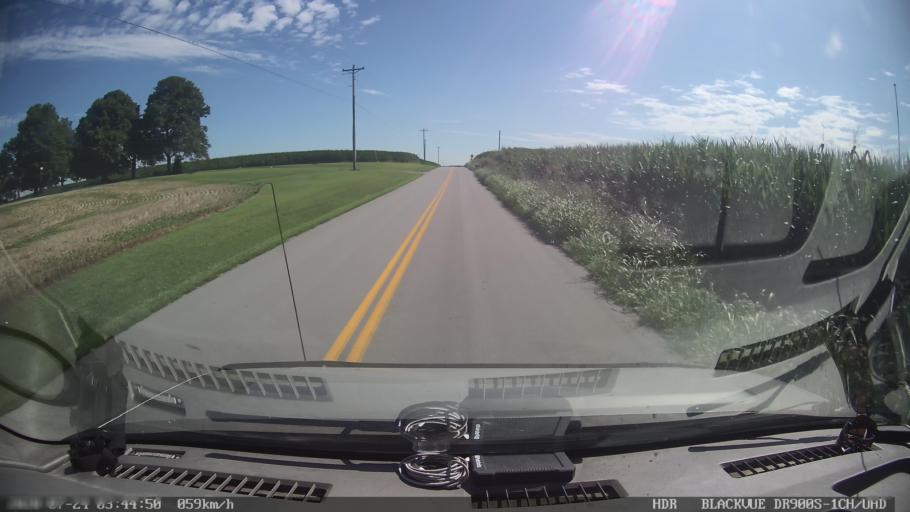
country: US
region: Kentucky
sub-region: Todd County
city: Elkton
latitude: 36.7446
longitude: -87.2283
